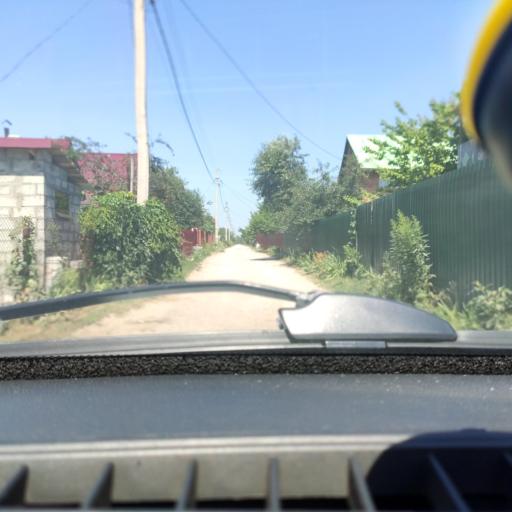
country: RU
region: Samara
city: Tol'yatti
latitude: 53.5924
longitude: 49.3040
